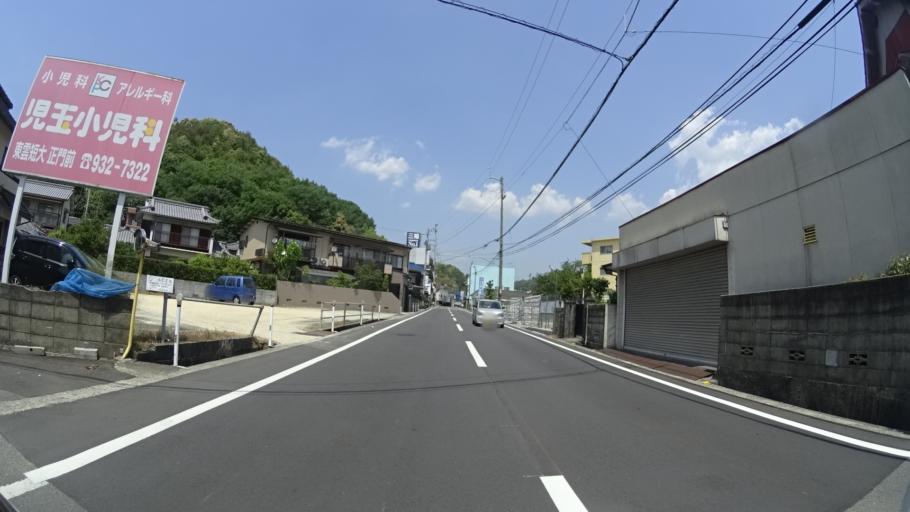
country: JP
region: Ehime
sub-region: Shikoku-chuo Shi
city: Matsuyama
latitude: 33.8473
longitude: 132.7988
